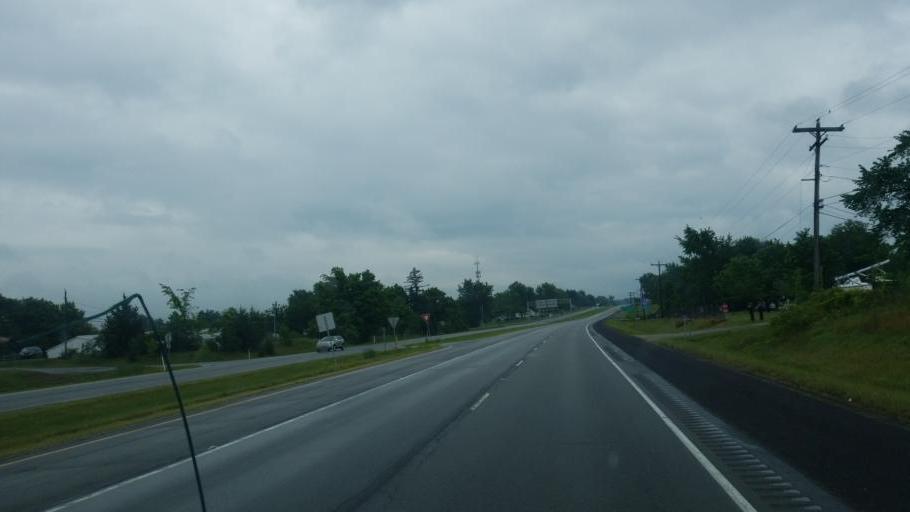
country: US
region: Indiana
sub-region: Allen County
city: New Haven
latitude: 40.9779
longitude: -85.0831
